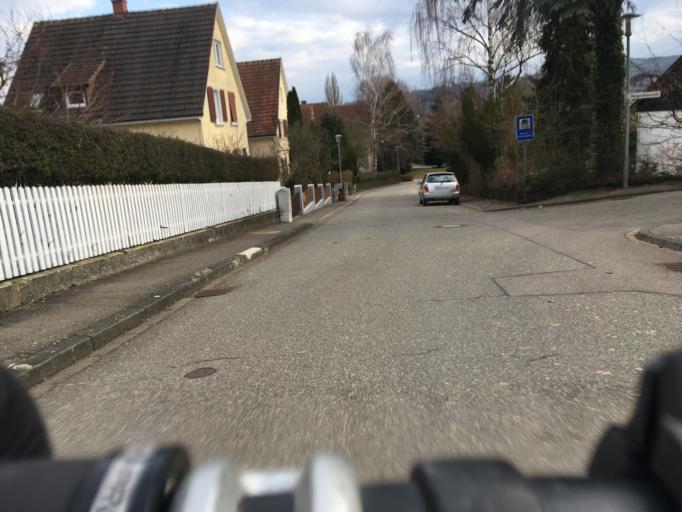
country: DE
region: Baden-Wuerttemberg
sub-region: Freiburg Region
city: Gottmadingen
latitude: 47.7332
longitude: 8.7715
